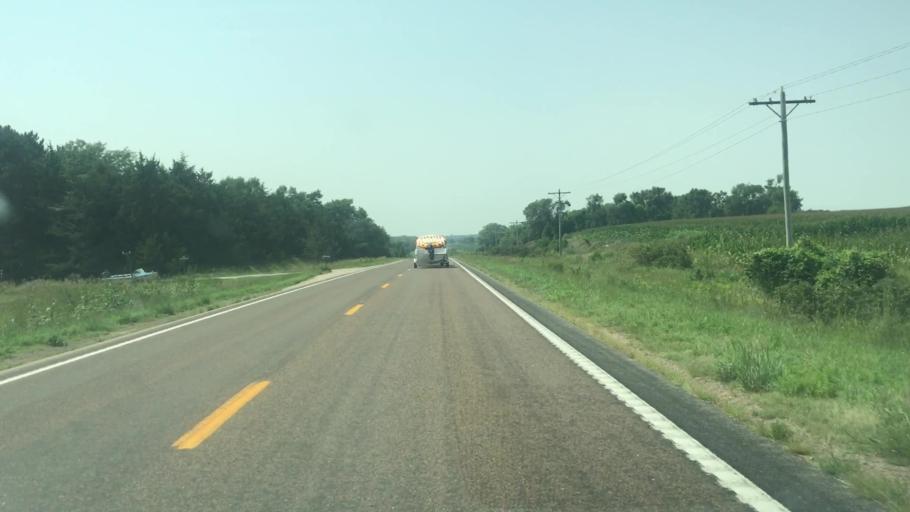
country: US
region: Nebraska
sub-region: Howard County
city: Saint Paul
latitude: 41.0760
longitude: -98.6643
